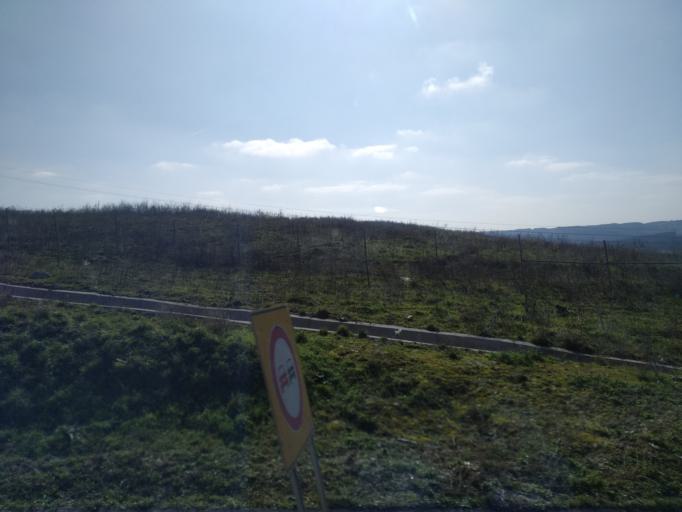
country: TR
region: Istanbul
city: Kemerburgaz
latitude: 41.2305
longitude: 28.8495
